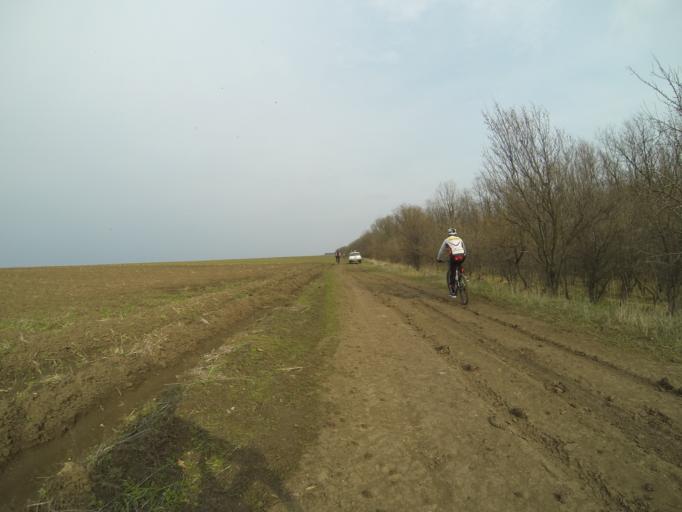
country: RO
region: Dolj
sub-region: Comuna Bucovat
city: Bucovat
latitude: 44.2596
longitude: 23.6942
